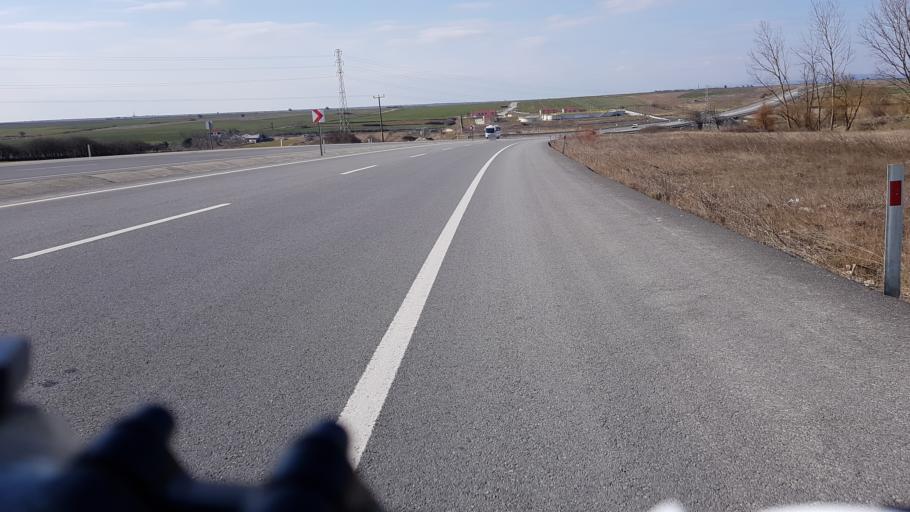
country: TR
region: Tekirdag
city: Saray
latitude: 41.4220
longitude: 27.9160
